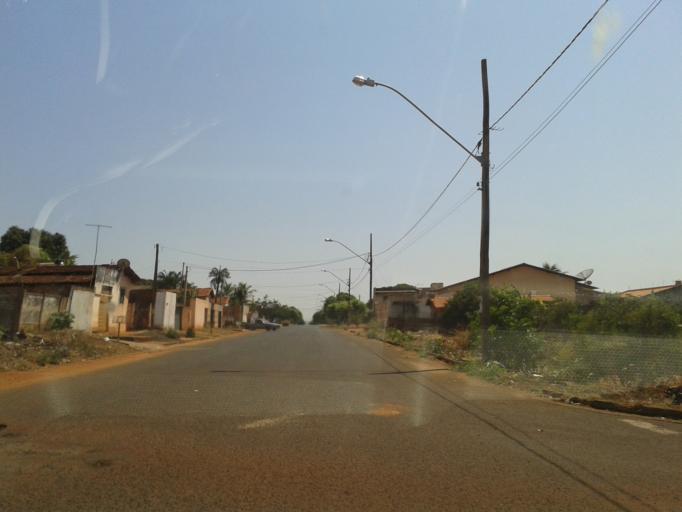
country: BR
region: Minas Gerais
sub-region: Ituiutaba
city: Ituiutaba
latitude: -18.9940
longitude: -49.4447
